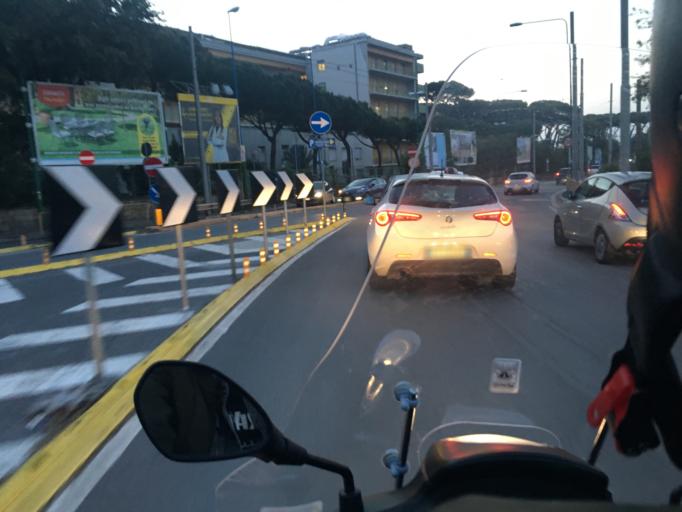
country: IT
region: Campania
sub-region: Provincia di Napoli
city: Napoli
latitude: 40.8662
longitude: 14.2271
